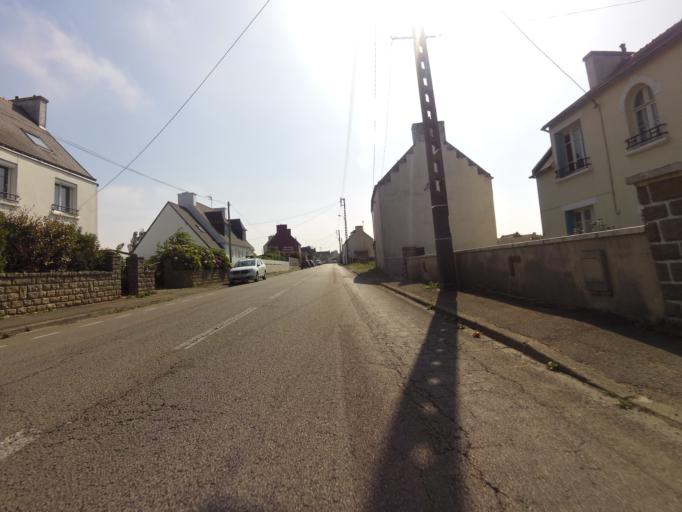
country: FR
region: Brittany
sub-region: Departement du Finistere
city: Plouhinec
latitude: 48.0157
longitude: -4.5104
